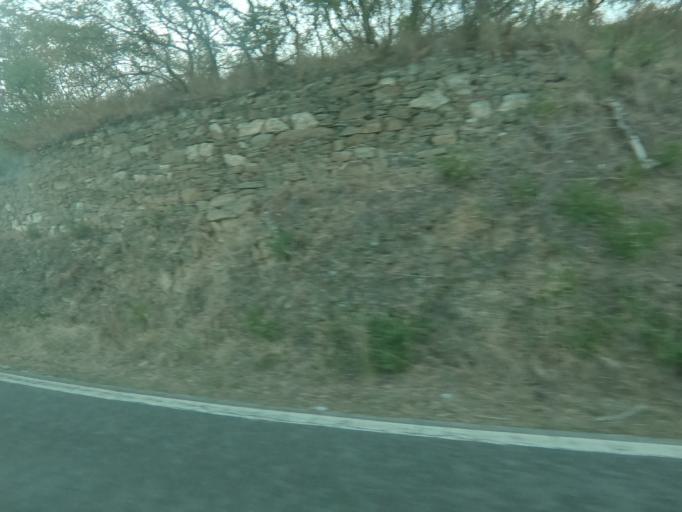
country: PT
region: Vila Real
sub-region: Peso da Regua
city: Peso da Regua
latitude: 41.1337
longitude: -7.7657
